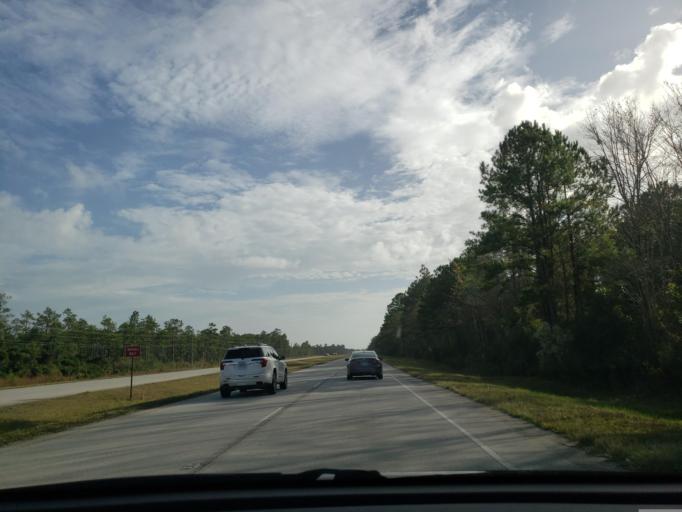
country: US
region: North Carolina
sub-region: Onslow County
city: Sneads Ferry
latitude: 34.6097
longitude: -77.4834
